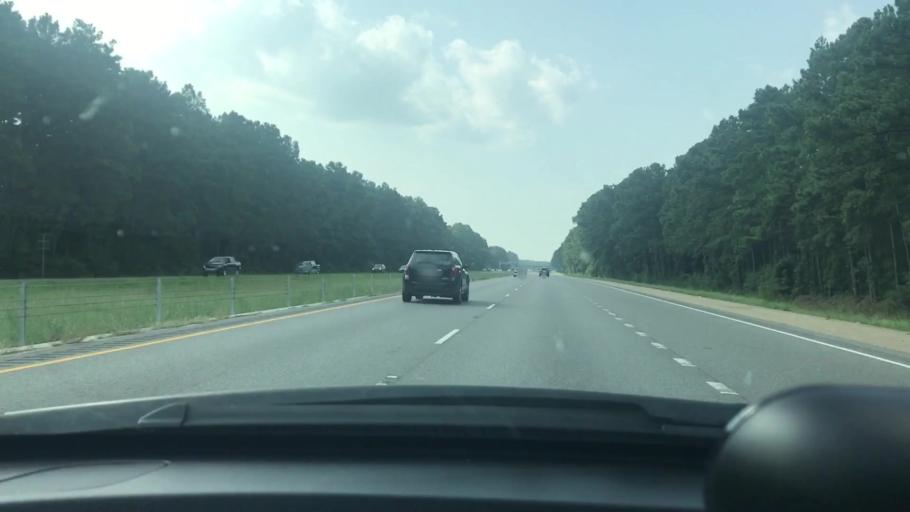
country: US
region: Louisiana
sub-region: Tangipahoa Parish
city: Hammond
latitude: 30.4830
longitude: -90.4918
